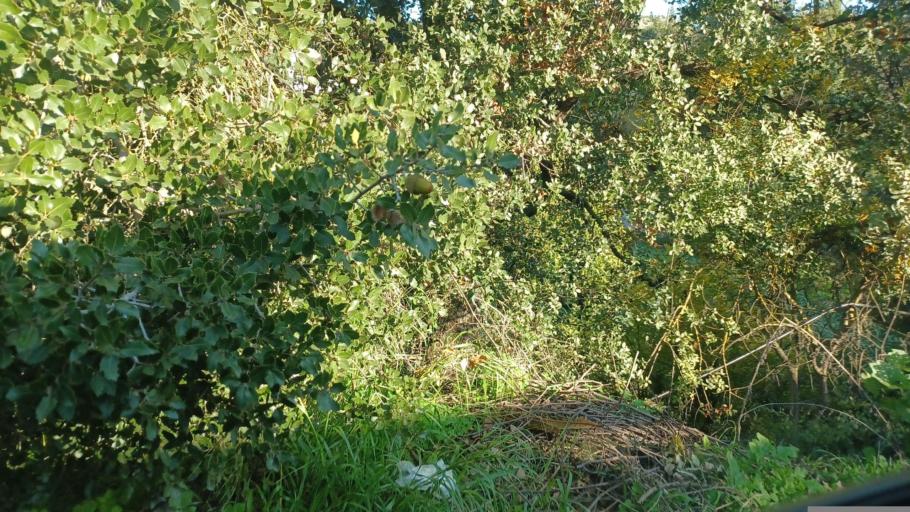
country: CY
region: Pafos
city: Mesogi
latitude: 34.8705
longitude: 32.5595
